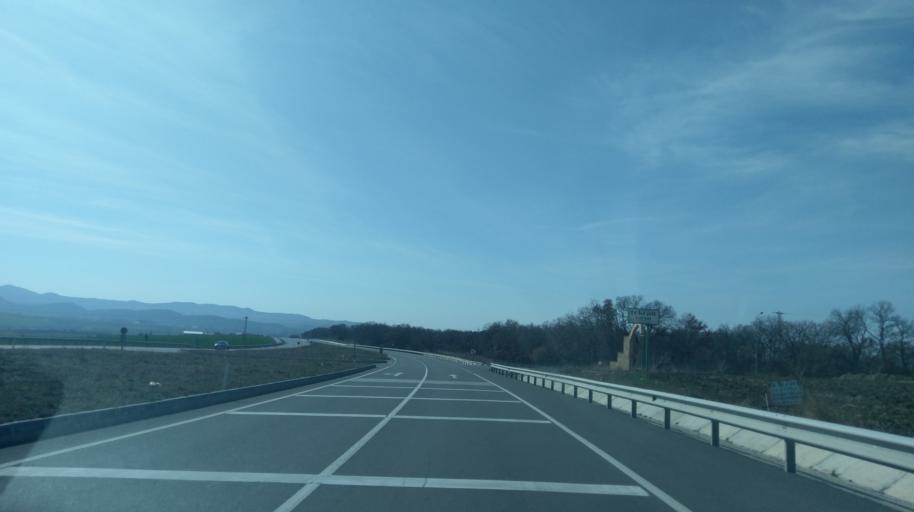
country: TR
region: Edirne
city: Kesan
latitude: 40.9063
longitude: 26.6316
